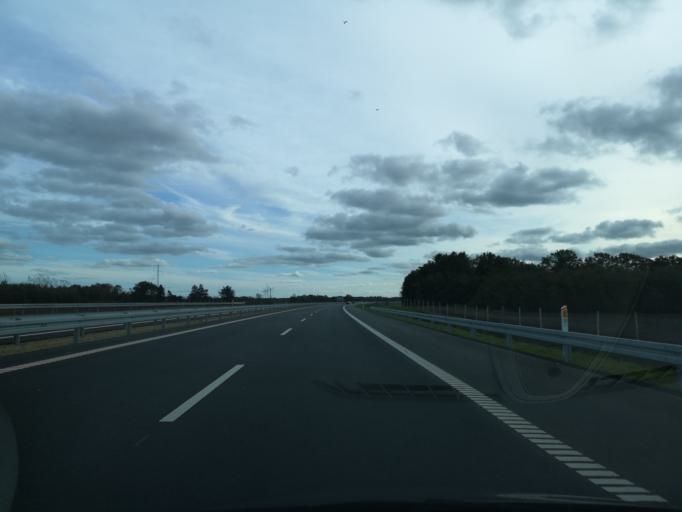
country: DK
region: Central Jutland
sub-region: Herning Kommune
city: Avlum
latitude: 56.3569
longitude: 8.7338
